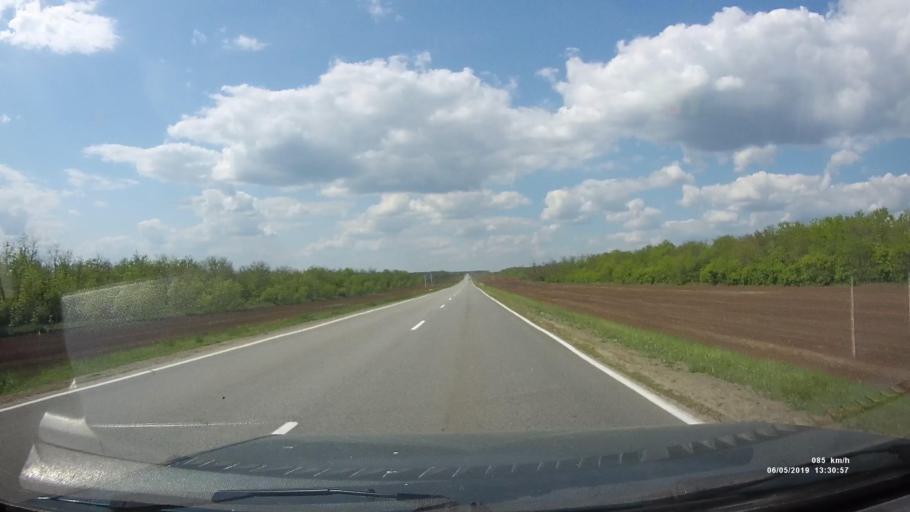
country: RU
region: Rostov
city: Ust'-Donetskiy
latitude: 47.6732
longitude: 40.8178
